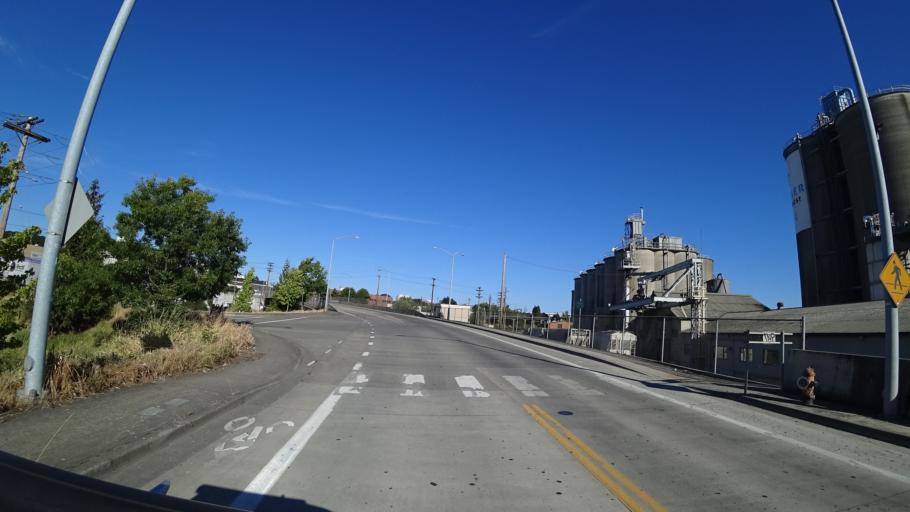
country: US
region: Oregon
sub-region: Multnomah County
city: Portland
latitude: 45.5380
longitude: -122.6775
